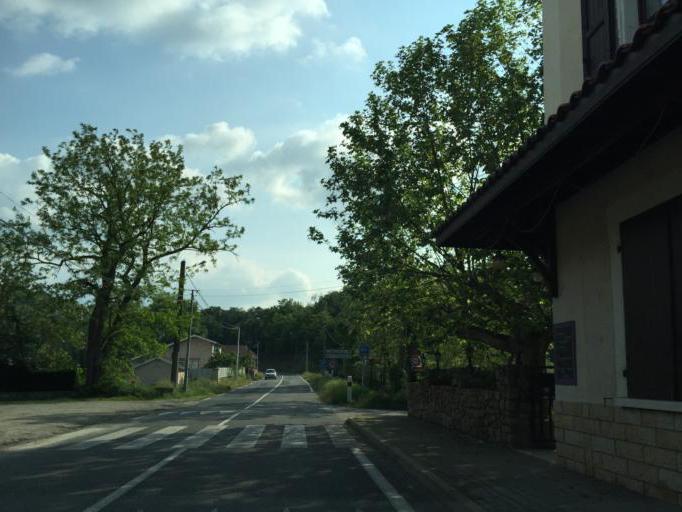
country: FR
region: Rhone-Alpes
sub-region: Departement du Rhone
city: Echalas
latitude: 45.5674
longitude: 4.7044
